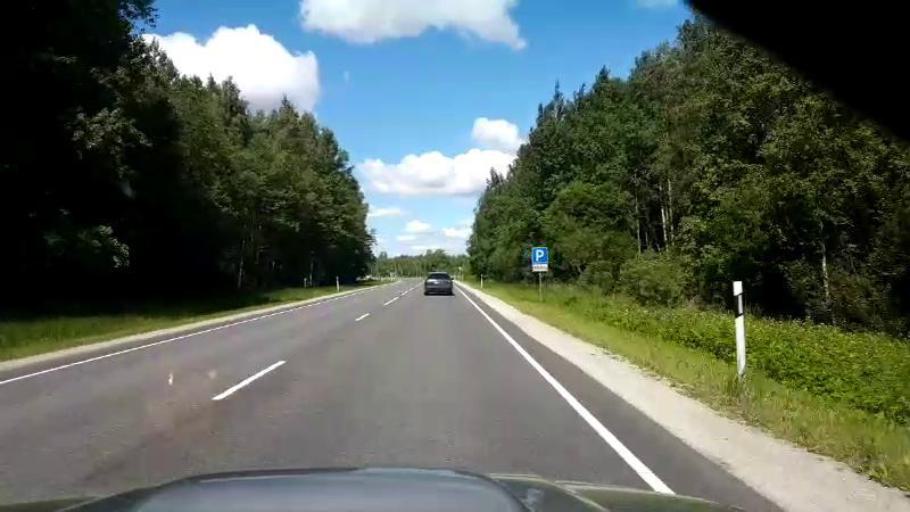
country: EE
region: Paernumaa
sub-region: Sauga vald
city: Sauga
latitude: 58.4435
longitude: 24.4987
